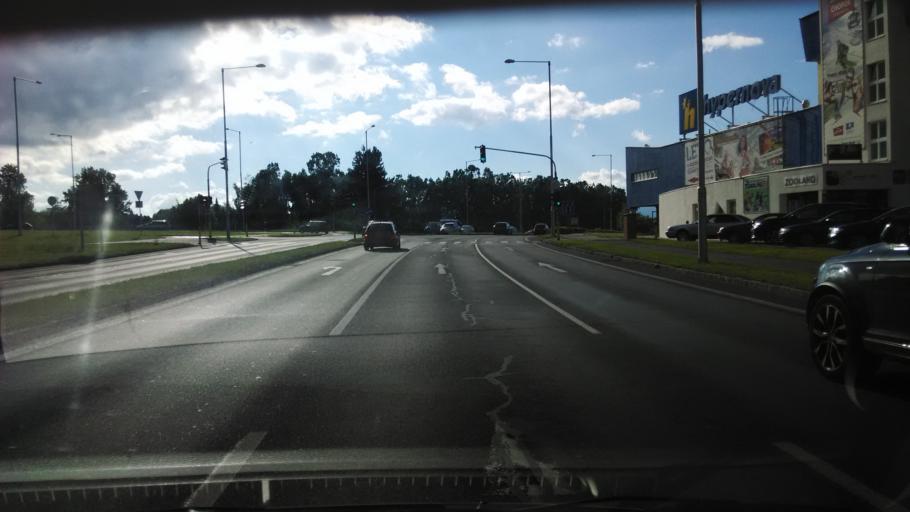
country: SK
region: Zilinsky
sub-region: Okres Liptovsky Mikulas
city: Liptovsky Mikulas
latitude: 49.0835
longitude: 19.6078
